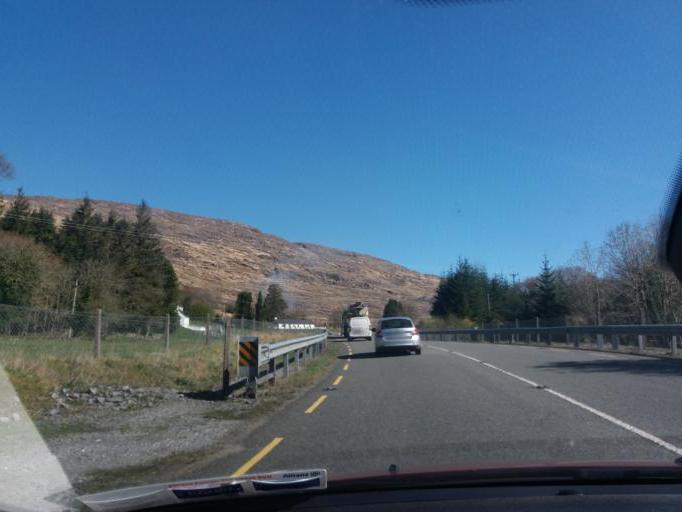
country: IE
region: Munster
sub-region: Ciarrai
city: Cill Airne
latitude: 51.9681
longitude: -9.3505
